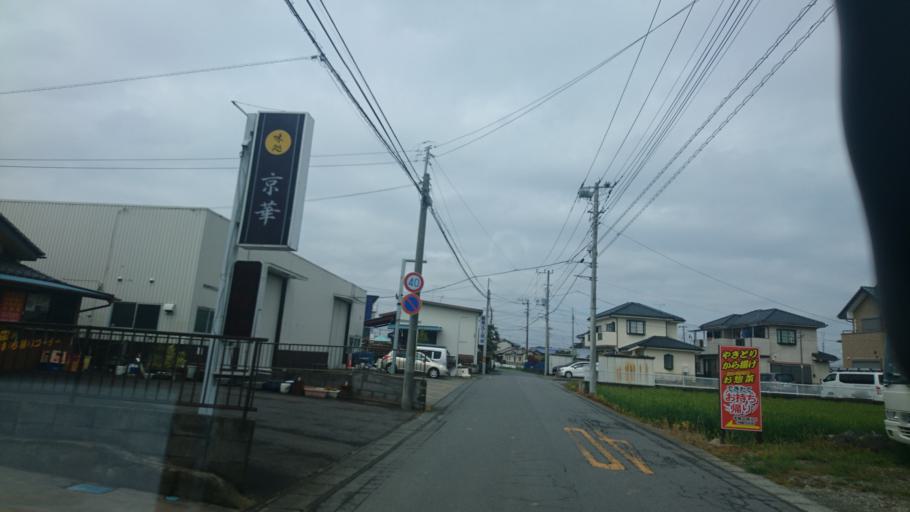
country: JP
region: Ibaraki
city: Mitsukaido
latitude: 36.0461
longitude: 139.9941
